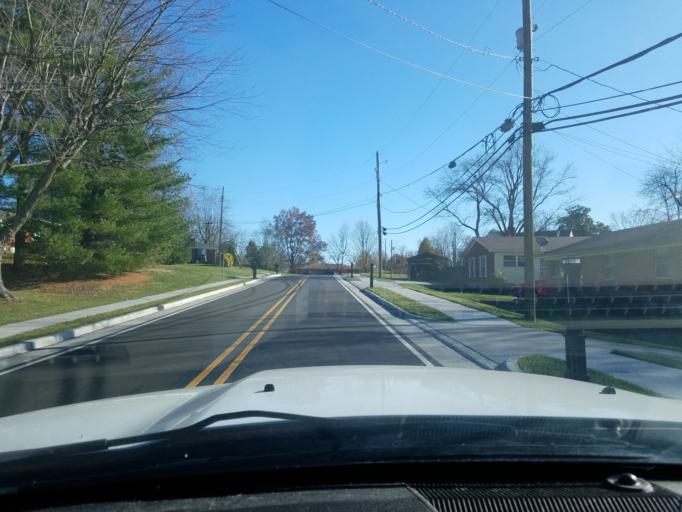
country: US
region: Indiana
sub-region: Floyd County
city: New Albany
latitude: 38.3220
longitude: -85.8144
